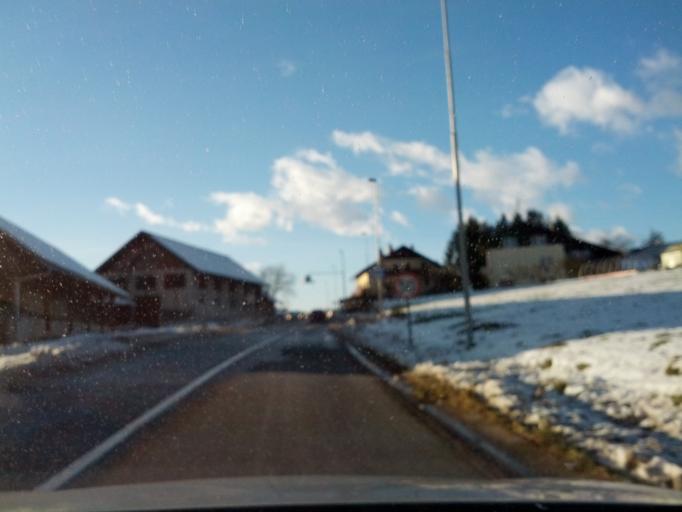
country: SI
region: Moravce
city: Moravce
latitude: 46.1373
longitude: 14.7200
